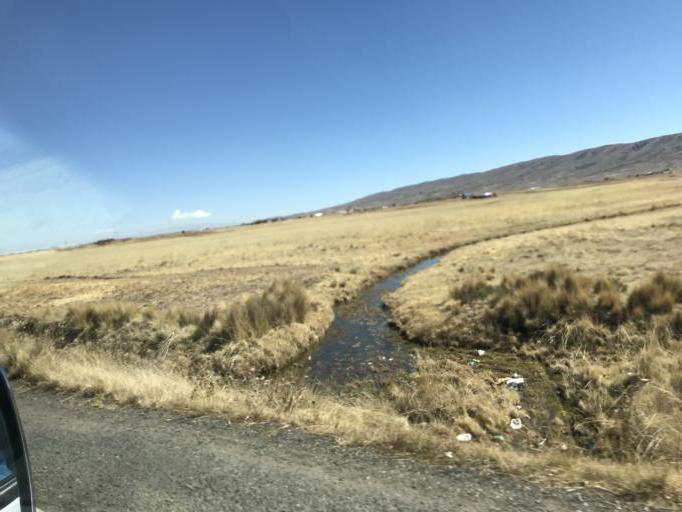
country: BO
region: La Paz
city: Tiahuanaco
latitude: -16.5692
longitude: -68.6620
